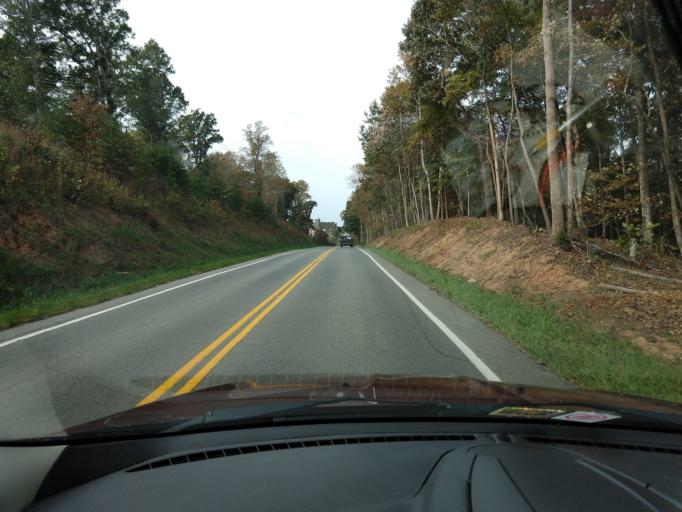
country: US
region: Virginia
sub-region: Franklin County
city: Union Hall
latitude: 36.9853
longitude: -79.6417
